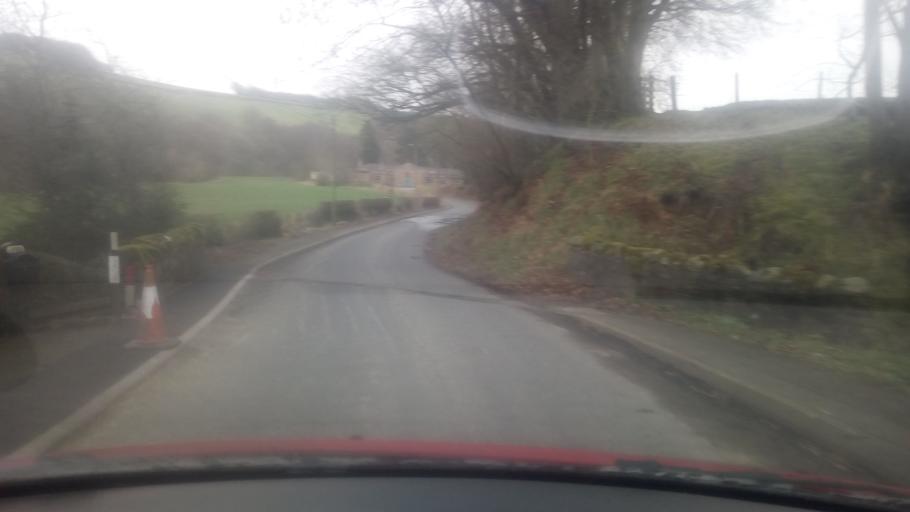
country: GB
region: Scotland
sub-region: The Scottish Borders
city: Hawick
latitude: 55.3942
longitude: -2.6568
